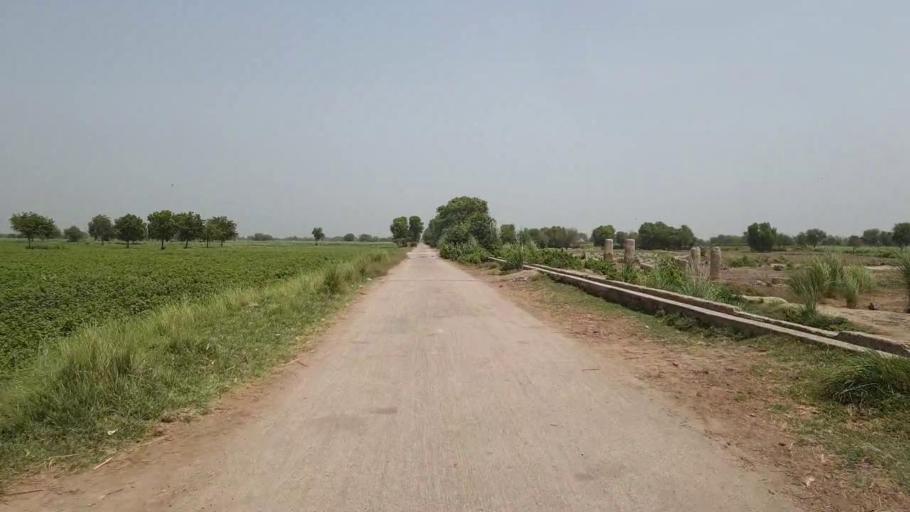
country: PK
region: Sindh
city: Nawabshah
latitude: 26.2892
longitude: 68.3090
